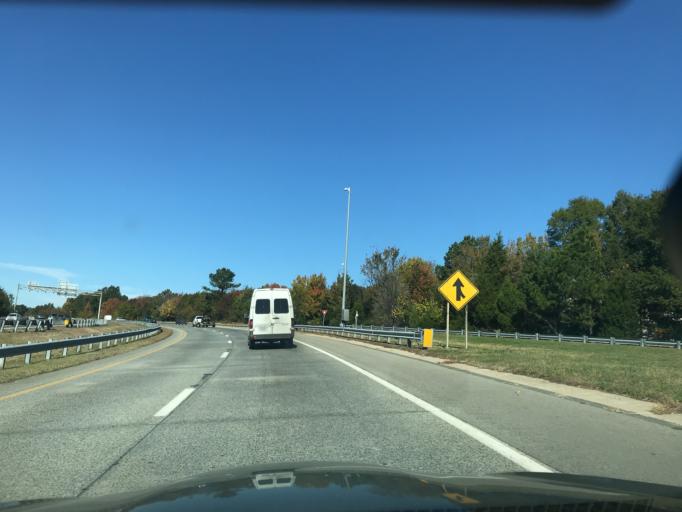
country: US
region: North Carolina
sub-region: Durham County
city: Durham
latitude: 35.9982
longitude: -78.9122
